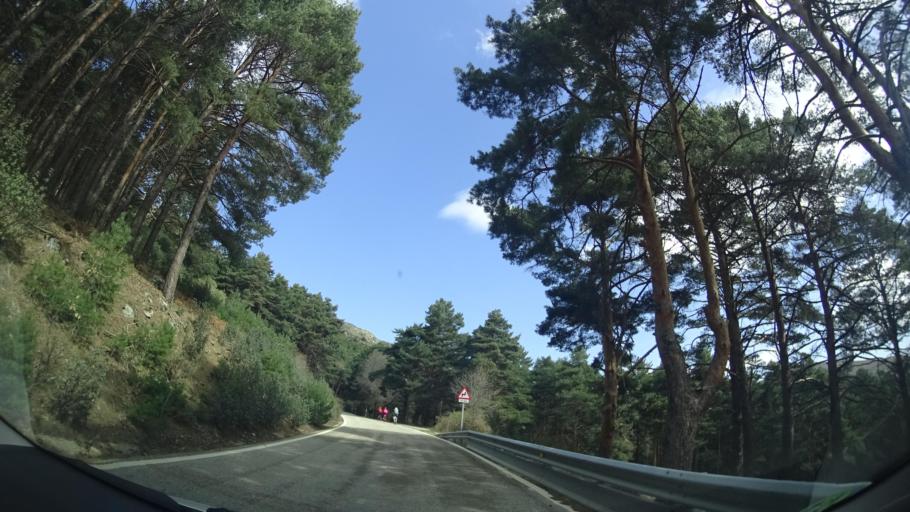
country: ES
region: Madrid
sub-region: Provincia de Madrid
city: Miraflores de la Sierra
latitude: 40.8557
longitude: -3.7659
